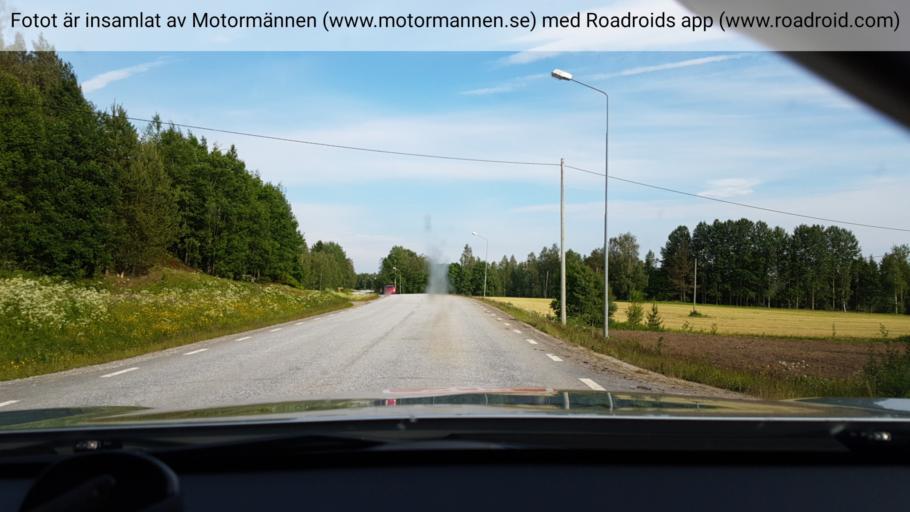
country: SE
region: Vaesterbotten
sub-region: Vindelns Kommun
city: Vindeln
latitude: 64.1309
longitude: 19.5381
